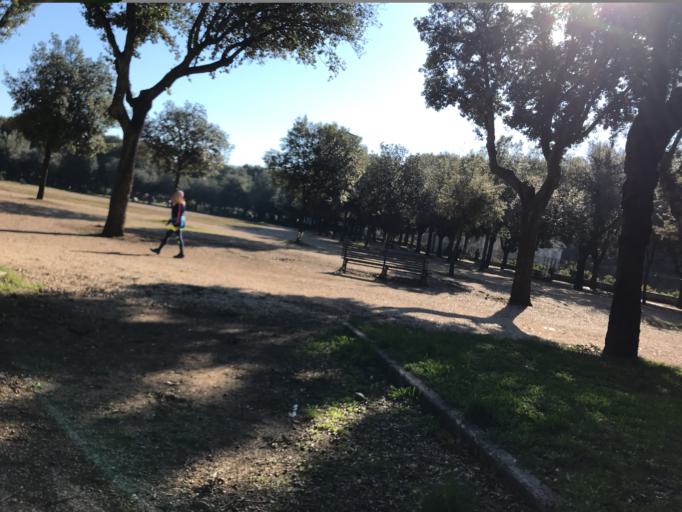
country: IT
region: Latium
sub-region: Citta metropolitana di Roma Capitale
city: Rome
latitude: 41.9157
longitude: 12.4905
